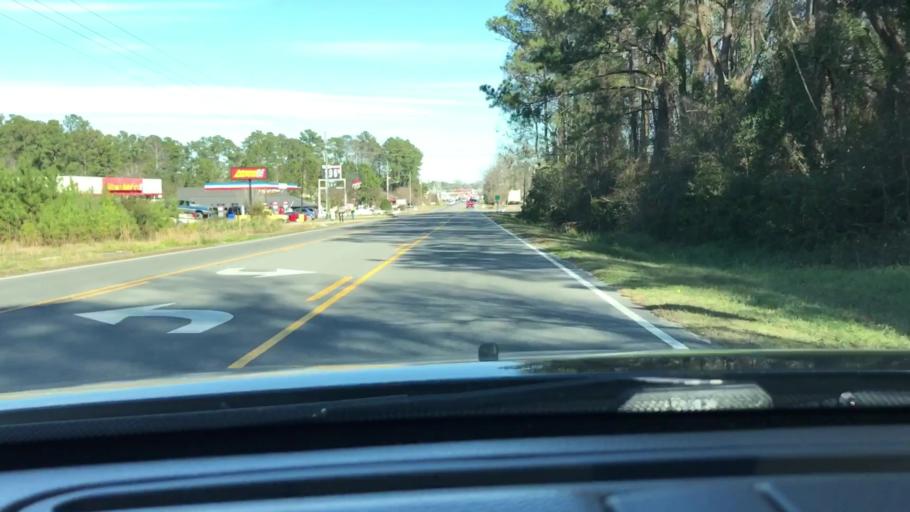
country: US
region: North Carolina
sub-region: Brunswick County
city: Shallotte
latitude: 33.9657
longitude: -78.3949
